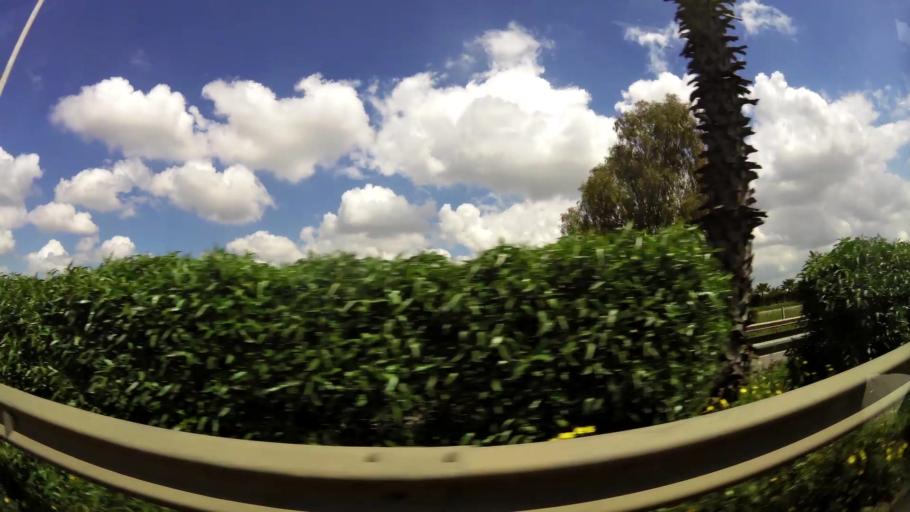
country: MA
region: Chaouia-Ouardigha
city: Nouaseur
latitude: 33.4063
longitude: -7.6245
